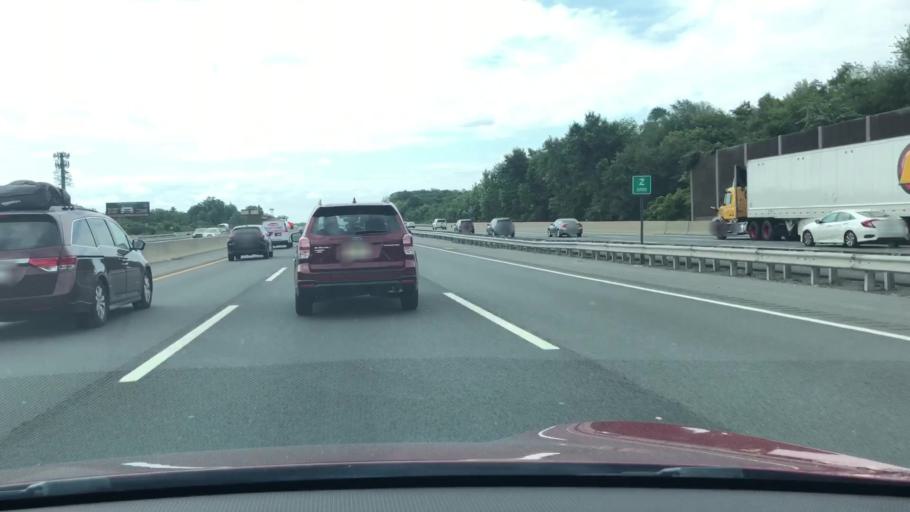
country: US
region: New Jersey
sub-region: Middlesex County
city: Milltown
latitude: 40.4573
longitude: -74.4199
